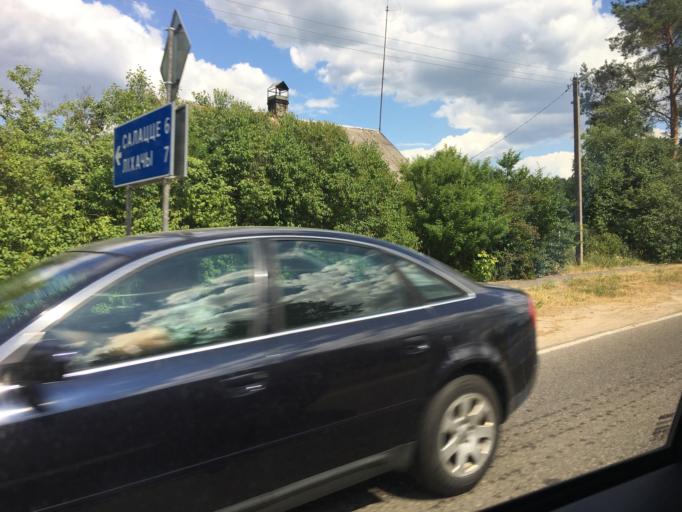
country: LT
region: Alytaus apskritis
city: Druskininkai
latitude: 53.8937
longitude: 24.1364
